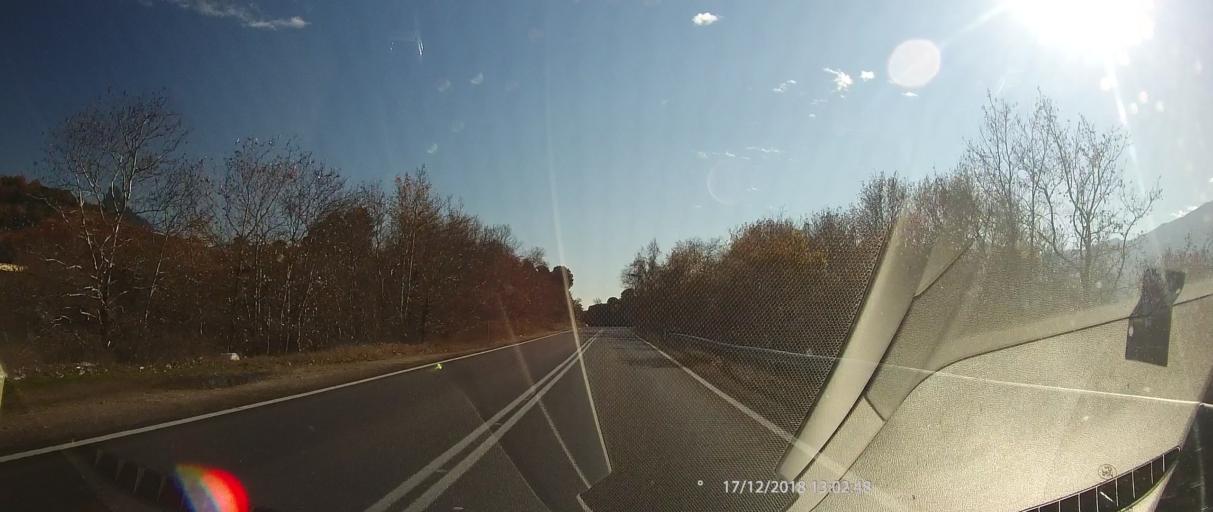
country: GR
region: Thessaly
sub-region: Trikala
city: Kastraki
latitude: 39.7190
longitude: 21.5953
